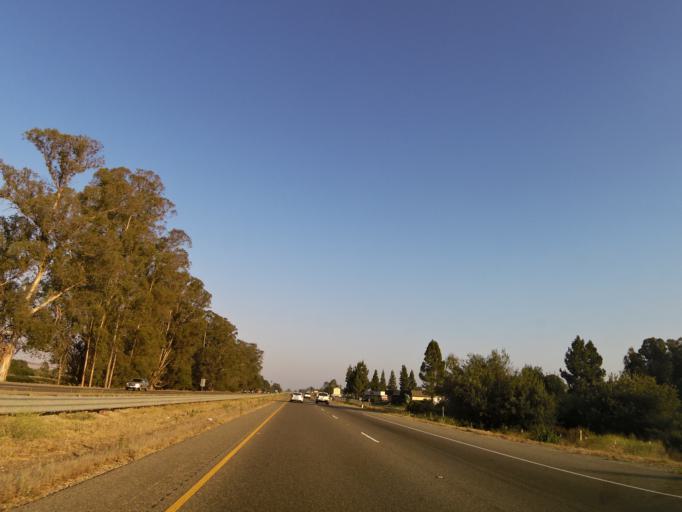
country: US
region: California
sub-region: San Luis Obispo County
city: Nipomo
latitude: 35.0468
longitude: -120.4937
